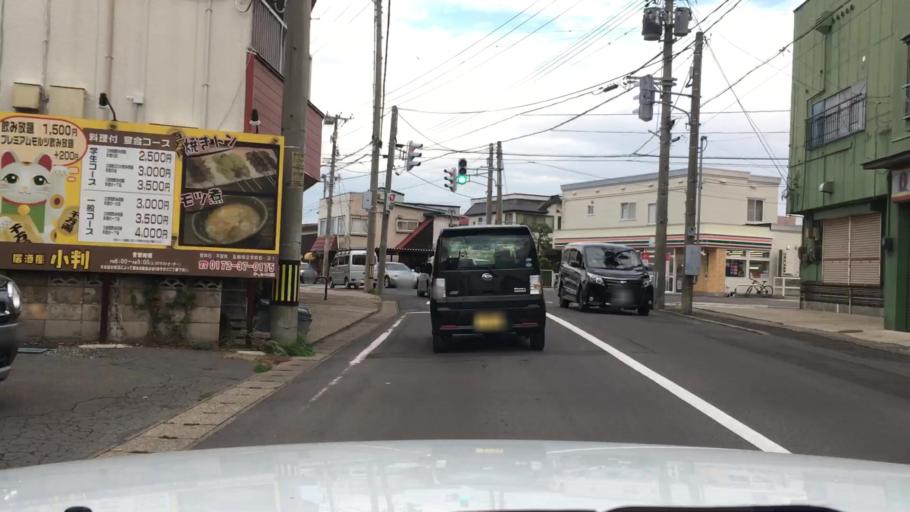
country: JP
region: Aomori
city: Hirosaki
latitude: 40.5850
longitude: 140.4707
